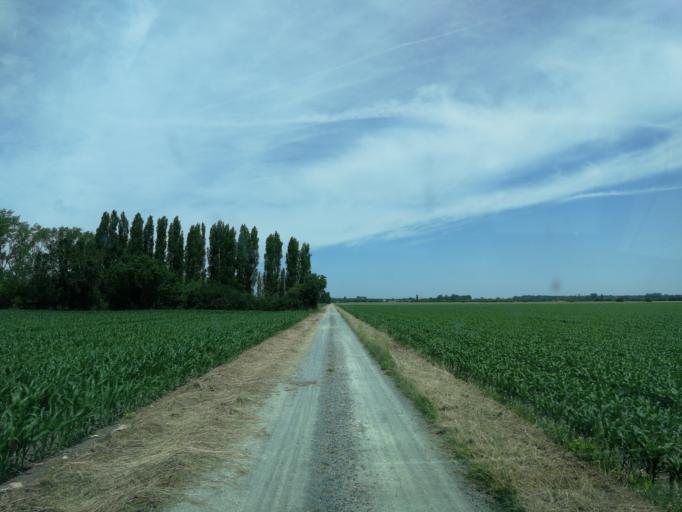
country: FR
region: Pays de la Loire
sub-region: Departement de la Vendee
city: Le Langon
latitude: 46.3692
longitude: -0.9586
